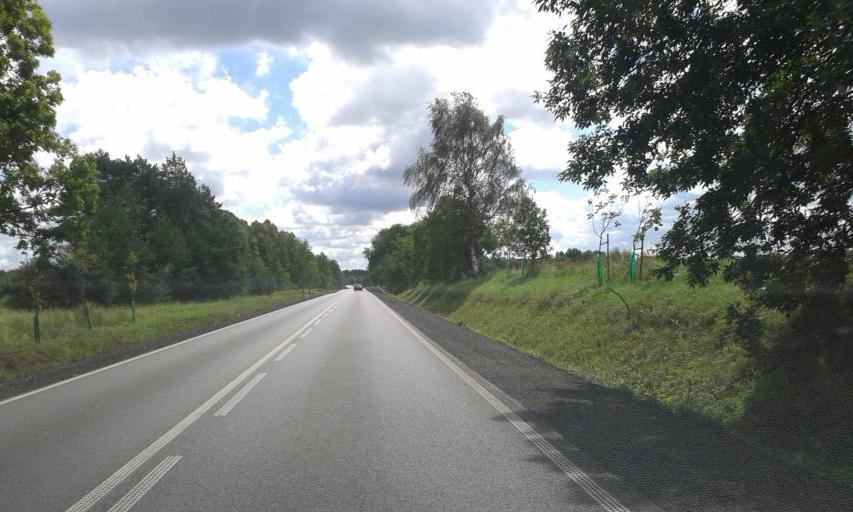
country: PL
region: West Pomeranian Voivodeship
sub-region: Powiat drawski
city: Czaplinek
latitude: 53.5383
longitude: 16.2739
